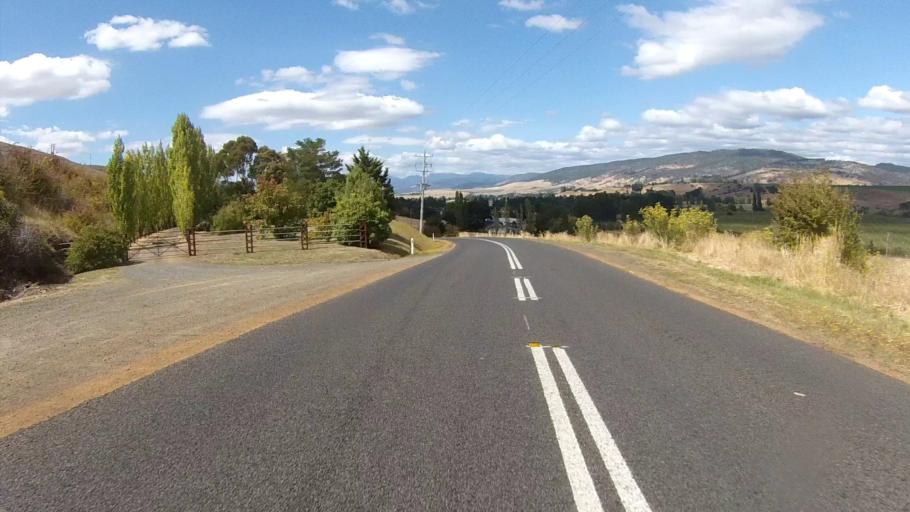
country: AU
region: Tasmania
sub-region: Derwent Valley
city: New Norfolk
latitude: -42.6914
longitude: 146.8836
